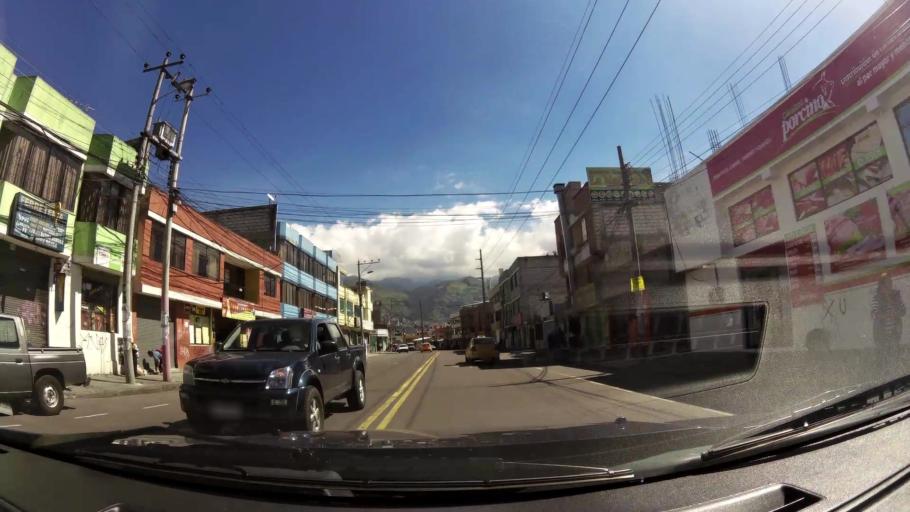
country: EC
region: Pichincha
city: Quito
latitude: -0.2616
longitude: -78.5384
